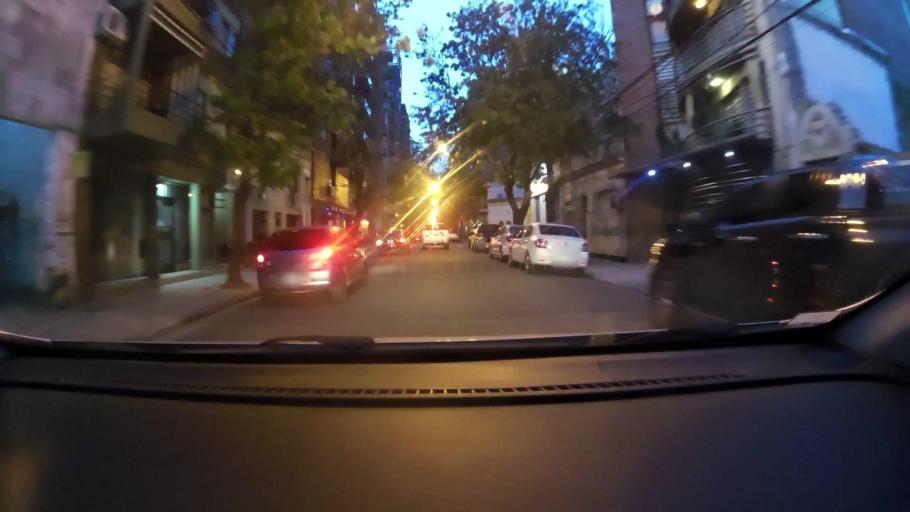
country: AR
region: Santa Fe
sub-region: Departamento de Rosario
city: Rosario
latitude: -32.9531
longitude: -60.6528
